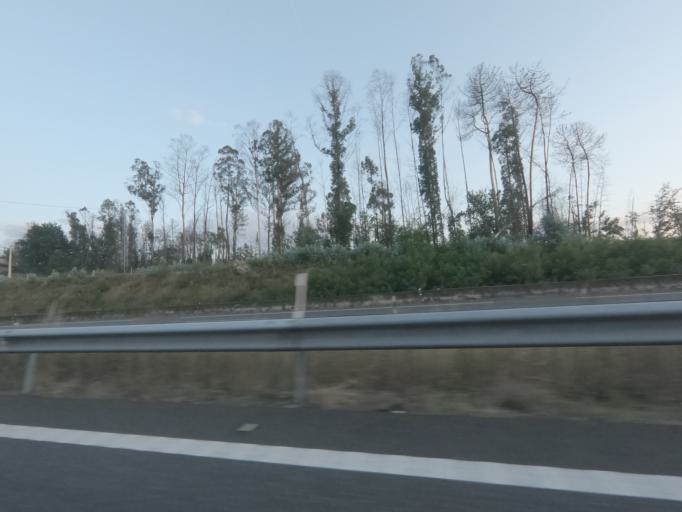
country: ES
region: Galicia
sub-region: Provincia de Pontevedra
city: Ponteareas
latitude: 42.1435
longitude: -8.4725
